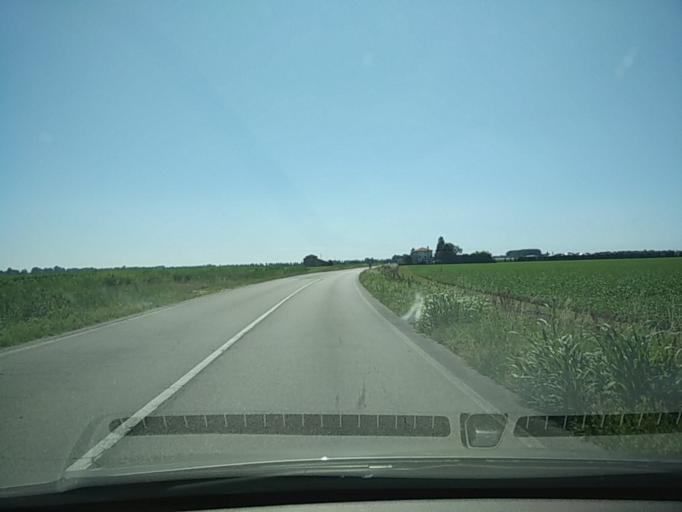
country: IT
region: Veneto
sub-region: Provincia di Venezia
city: San Giorgio di Livenza
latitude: 45.6352
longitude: 12.7657
